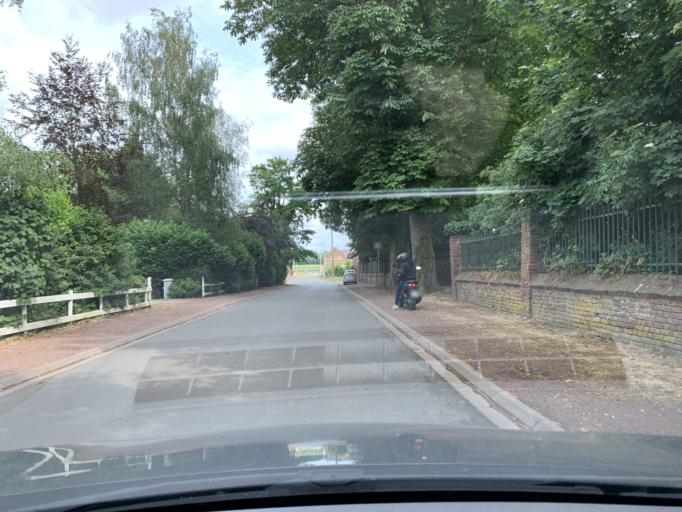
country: FR
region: Nord-Pas-de-Calais
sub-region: Departement du Nord
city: Guesnain
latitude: 50.3268
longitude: 3.1470
